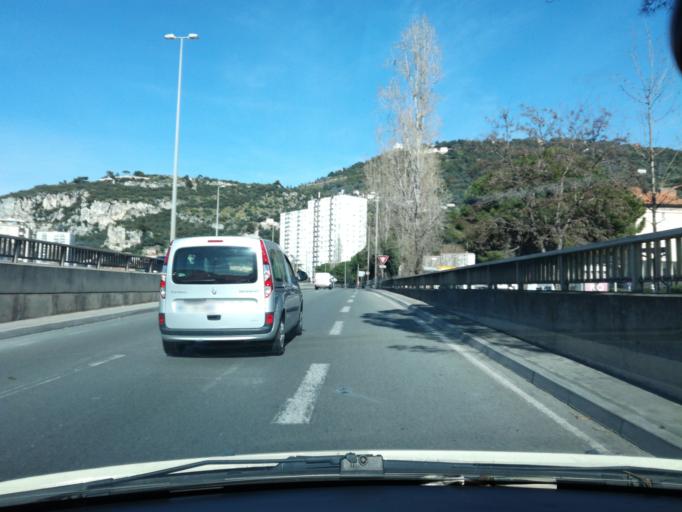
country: FR
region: Provence-Alpes-Cote d'Azur
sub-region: Departement des Alpes-Maritimes
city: Saint-Andre-de-la-Roche
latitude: 43.7196
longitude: 7.2858
